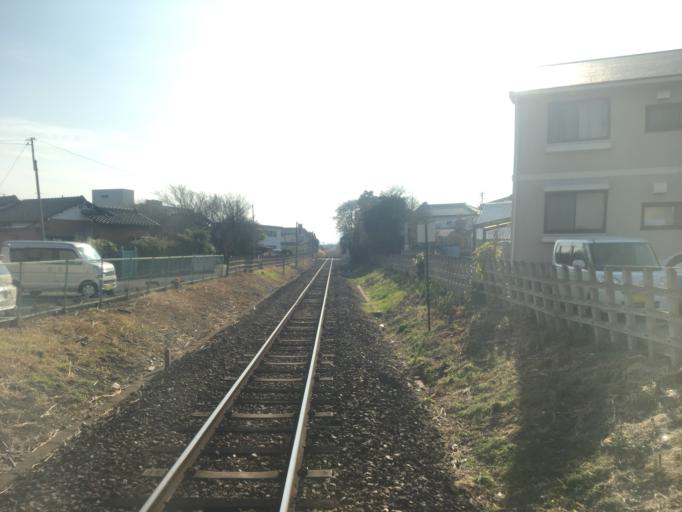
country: JP
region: Gunma
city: Fujioka
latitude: 36.2445
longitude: 139.0833
